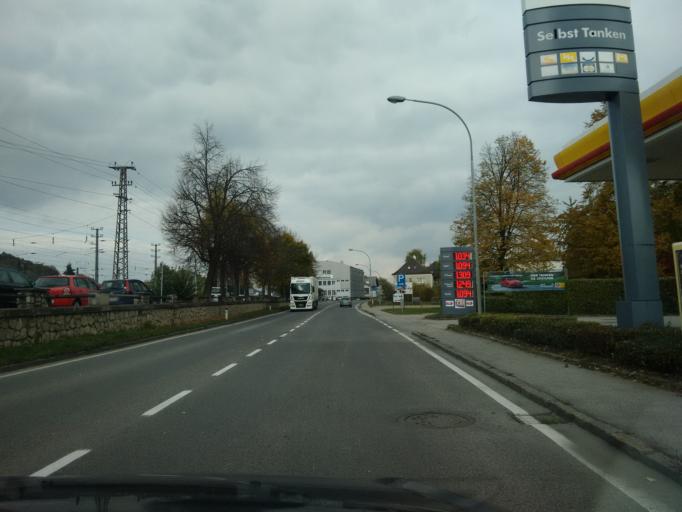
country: AT
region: Upper Austria
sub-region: Politischer Bezirk Vocklabruck
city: Attnang-Puchheim
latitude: 48.0145
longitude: 13.7233
